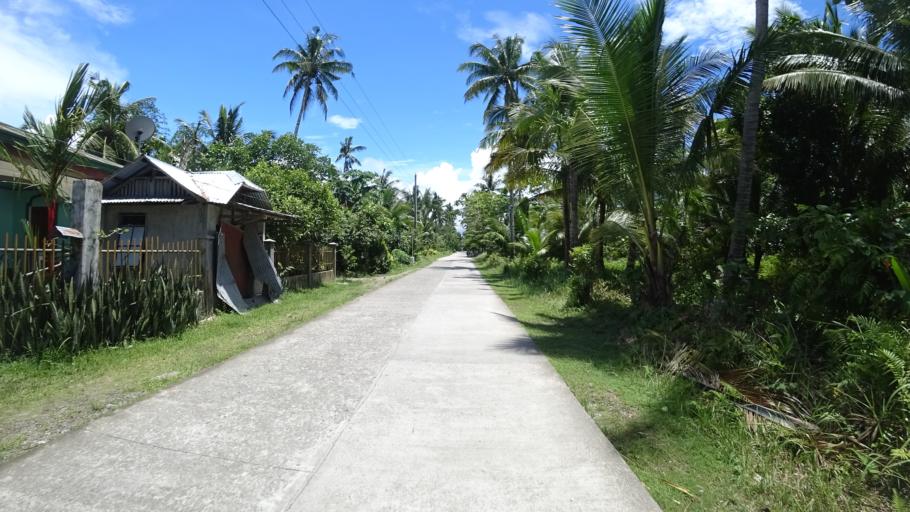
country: PH
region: Eastern Visayas
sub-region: Province of Leyte
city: Mayorga
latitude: 10.8927
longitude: 125.0047
